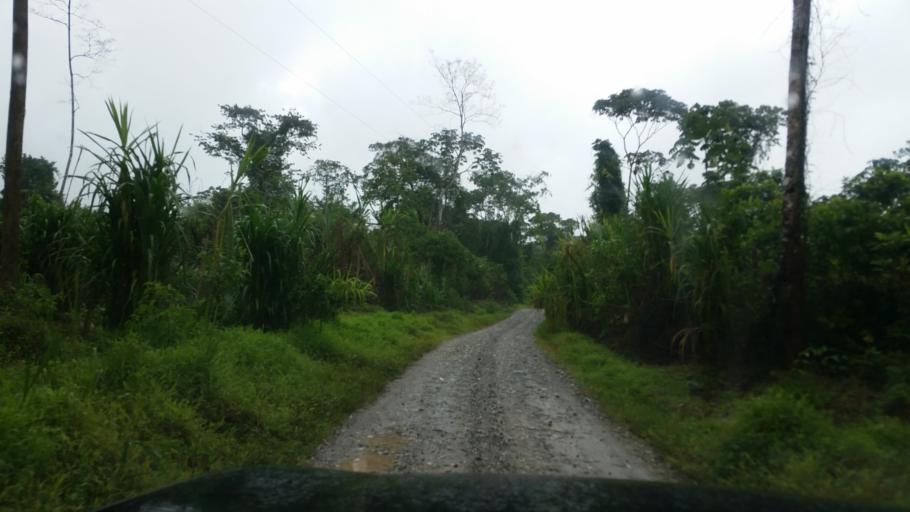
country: NI
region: Atlantico Norte (RAAN)
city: Bonanza
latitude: 14.0763
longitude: -84.6565
